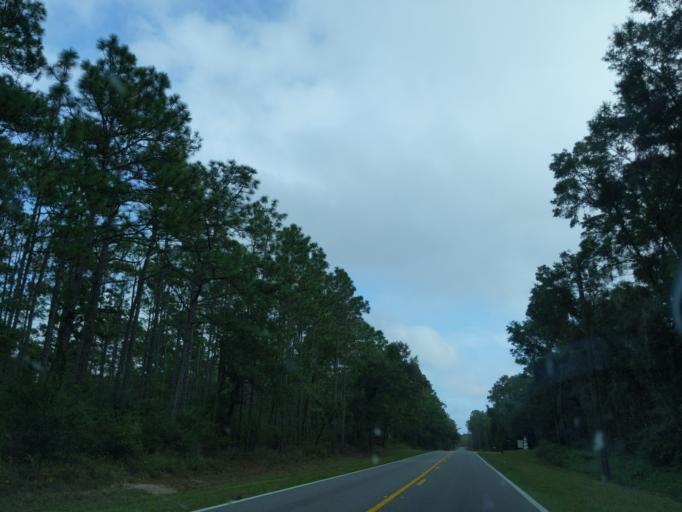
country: US
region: Florida
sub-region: Wakulla County
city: Crawfordville
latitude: 30.1191
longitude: -84.3142
